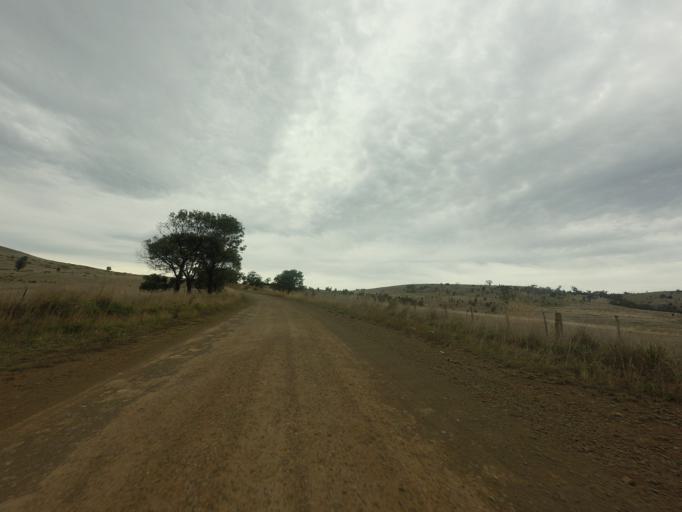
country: AU
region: Tasmania
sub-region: Derwent Valley
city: New Norfolk
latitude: -42.5563
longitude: 146.8892
